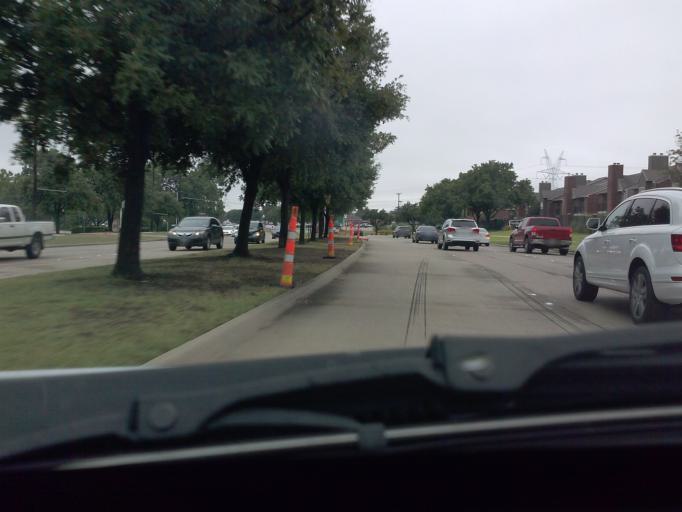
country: US
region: Texas
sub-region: Collin County
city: Plano
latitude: 33.0580
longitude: -96.7291
